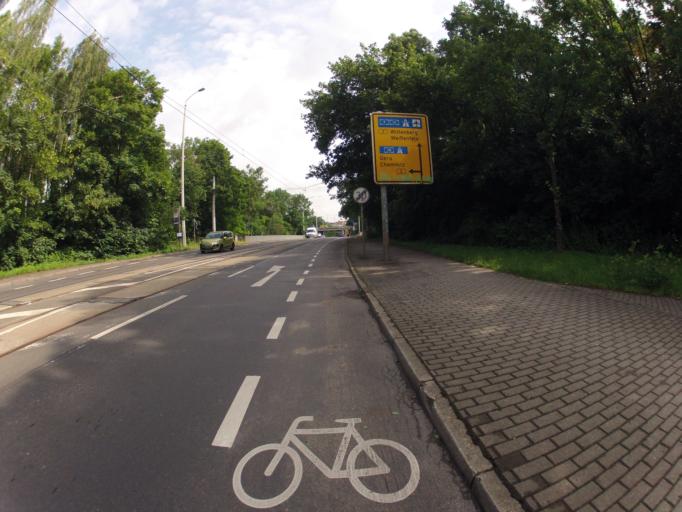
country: DE
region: Saxony
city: Markkleeberg
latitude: 51.3002
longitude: 12.3723
